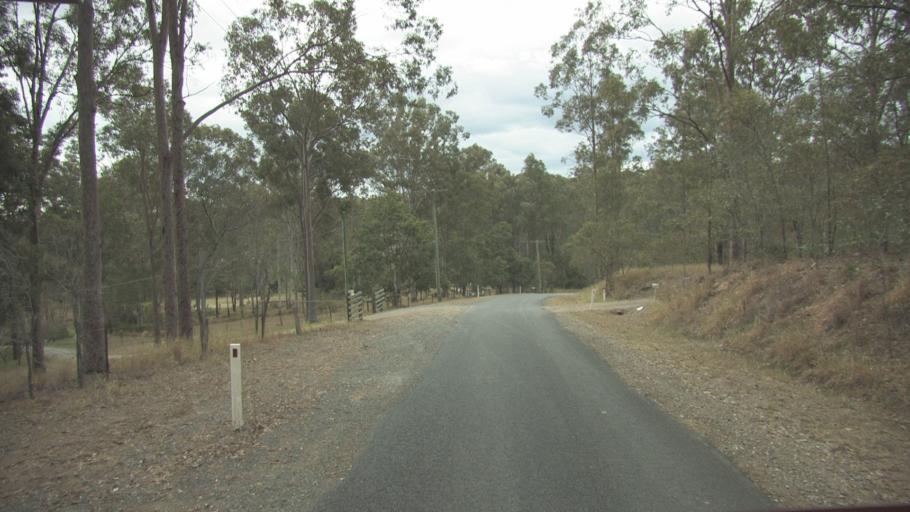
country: AU
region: Queensland
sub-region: Logan
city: Cedar Vale
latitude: -27.8564
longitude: 153.0652
